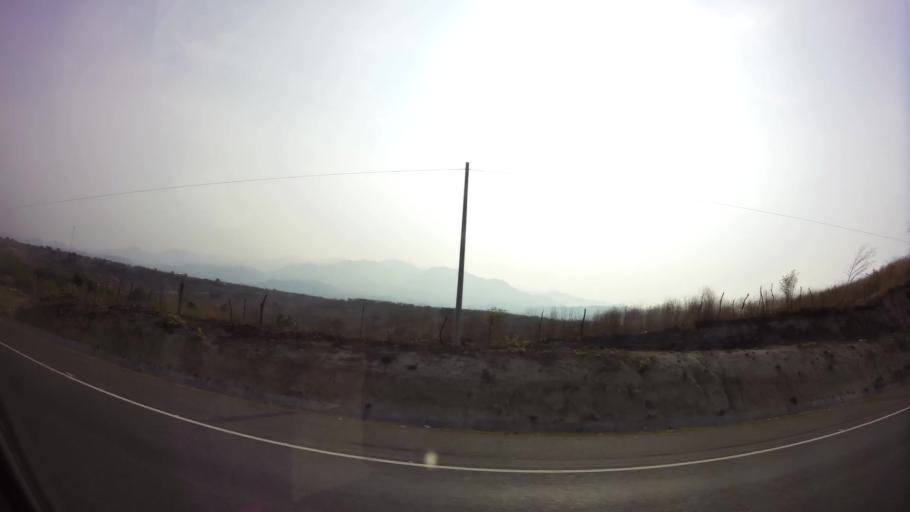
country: HN
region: Comayagua
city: Comayagua
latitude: 14.4110
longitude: -87.6226
